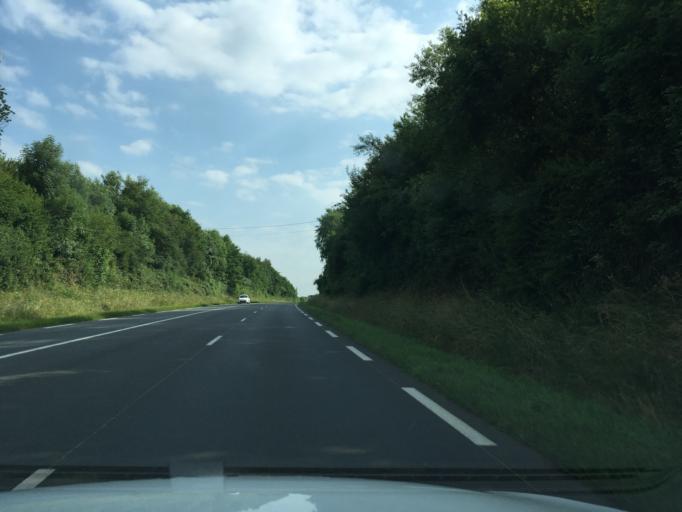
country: FR
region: Poitou-Charentes
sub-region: Departement des Deux-Sevres
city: Saint-Pardoux
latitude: 46.5780
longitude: -0.2934
